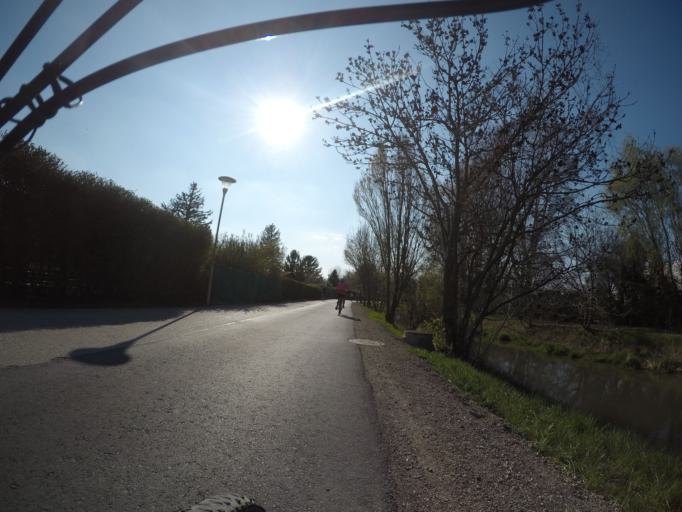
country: AT
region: Lower Austria
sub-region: Politischer Bezirk Modling
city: Neu-Guntramsdorf
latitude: 48.0577
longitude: 16.3255
